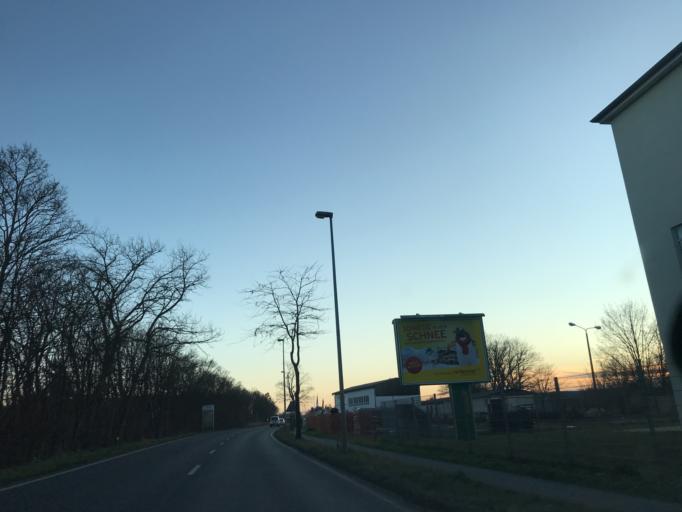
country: DE
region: Brandenburg
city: Rathenow
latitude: 52.5863
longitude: 12.3381
